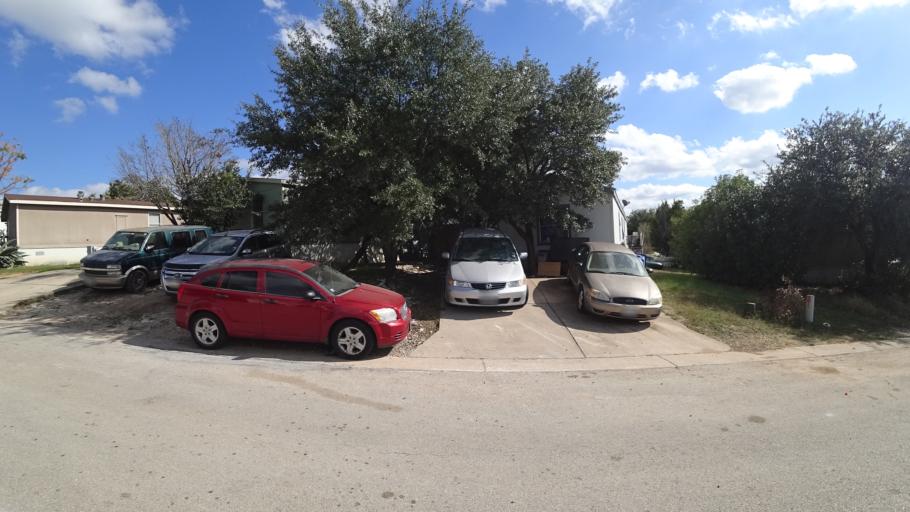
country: US
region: Texas
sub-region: Travis County
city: Barton Creek
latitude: 30.2488
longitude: -97.8834
